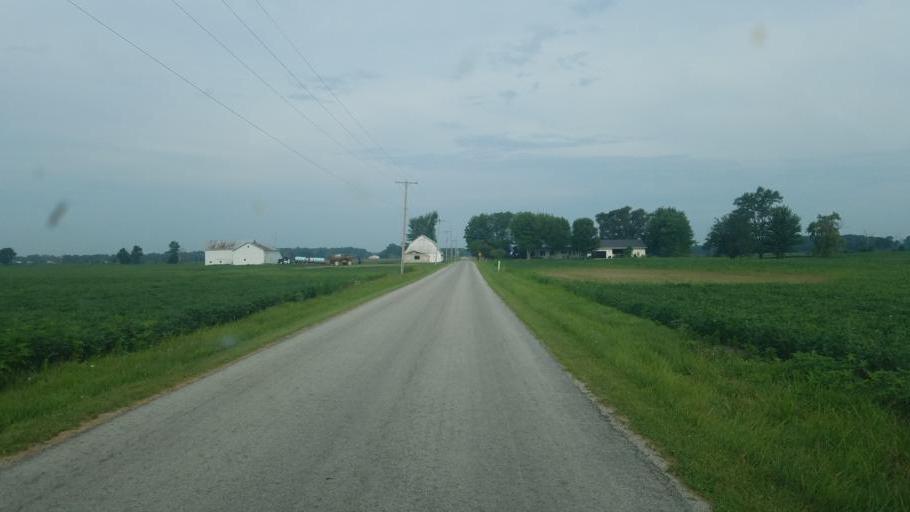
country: US
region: Ohio
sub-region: Morrow County
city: Cardington
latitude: 40.5164
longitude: -82.8818
